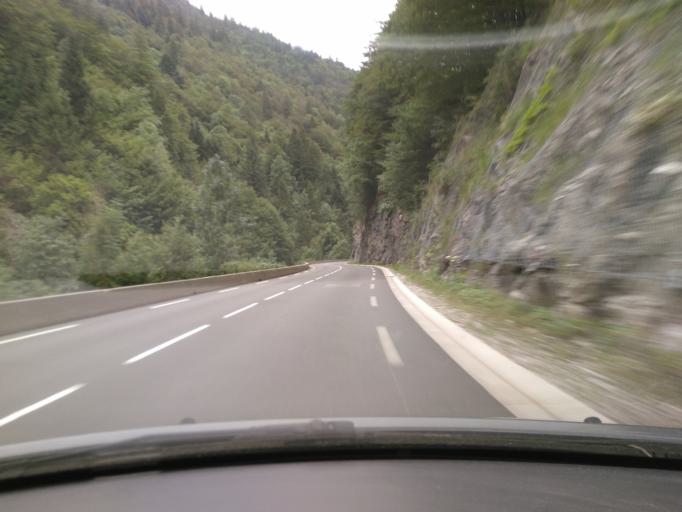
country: FR
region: Rhone-Alpes
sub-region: Departement de la Haute-Savoie
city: Saint-Jean-de-Sixt
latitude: 45.9337
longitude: 6.4010
